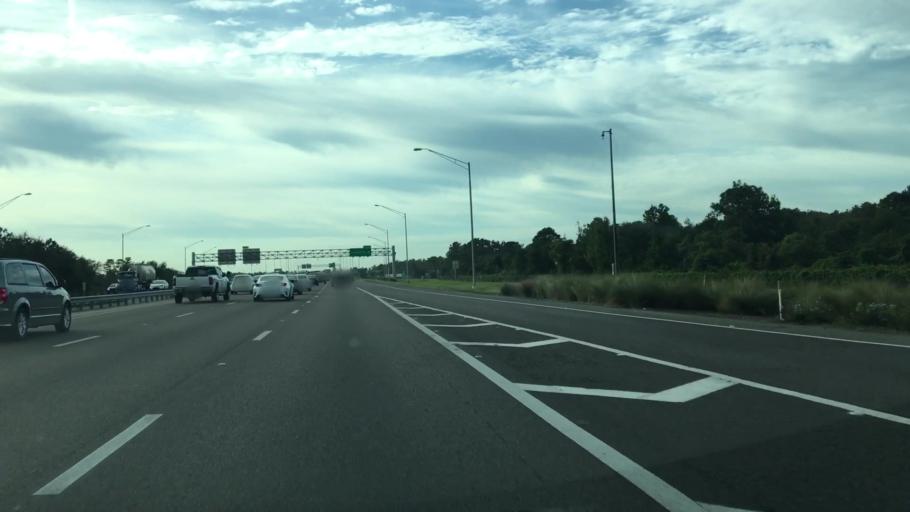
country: US
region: Florida
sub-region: Orange County
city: Azalea Park
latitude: 28.4848
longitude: -81.2415
